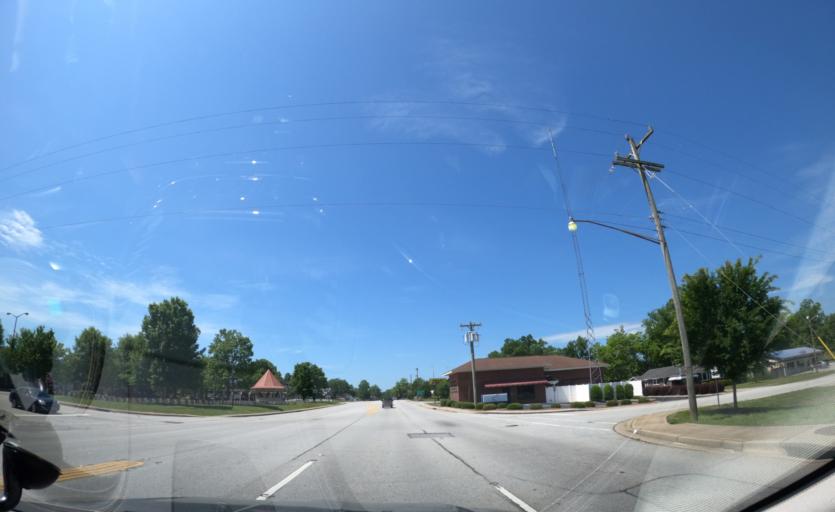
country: US
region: South Carolina
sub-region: Anderson County
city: Iva
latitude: 34.3068
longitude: -82.6638
